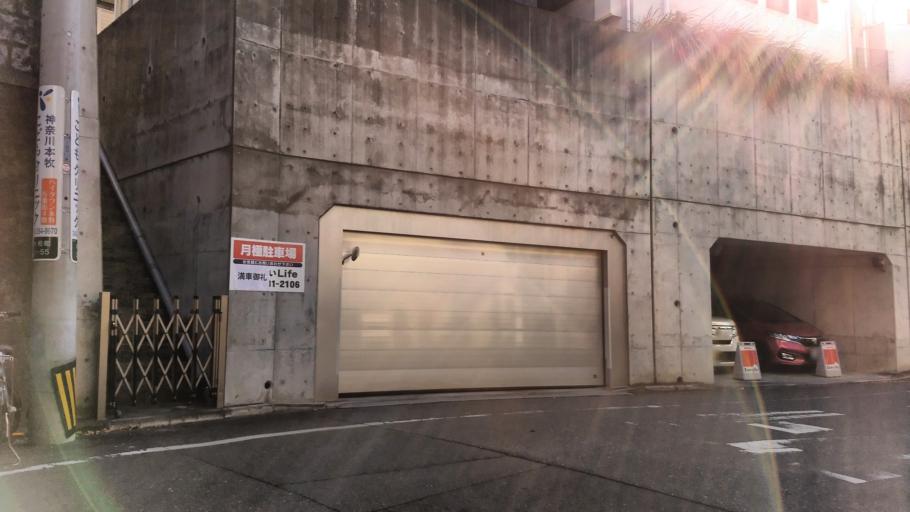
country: JP
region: Kanagawa
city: Yokohama
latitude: 35.4281
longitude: 139.6465
